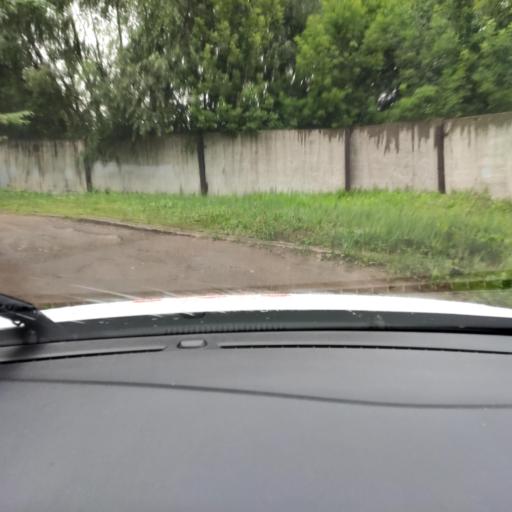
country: RU
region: Tatarstan
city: Vysokaya Gora
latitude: 55.8760
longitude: 49.2373
